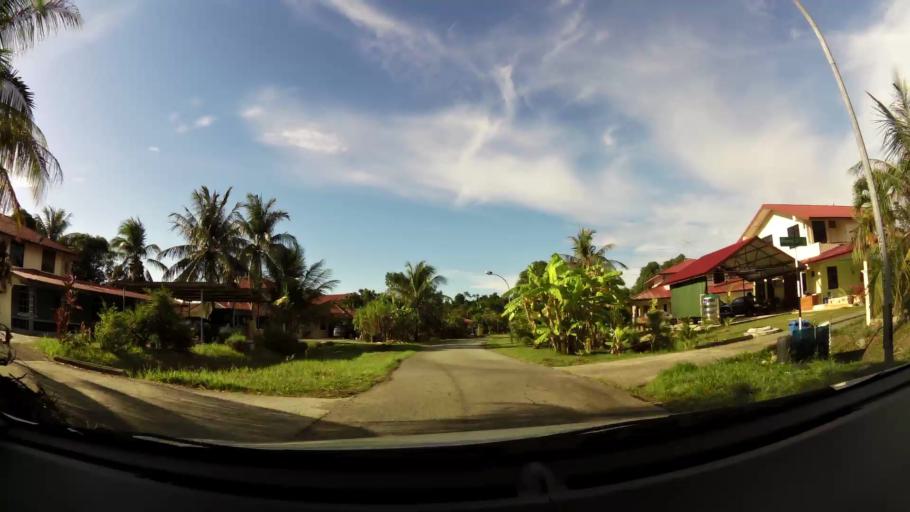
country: BN
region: Brunei and Muara
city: Bandar Seri Begawan
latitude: 4.9795
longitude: 114.9646
